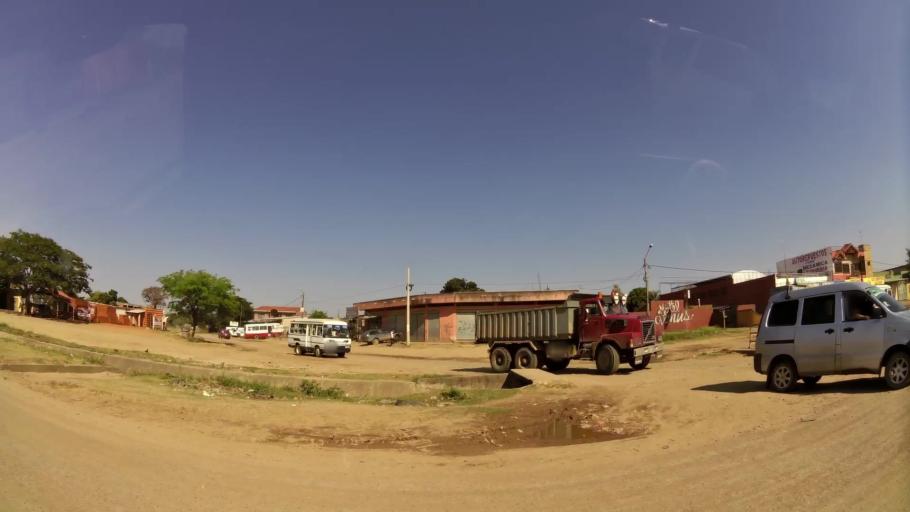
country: BO
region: Santa Cruz
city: Cotoca
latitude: -17.8162
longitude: -63.1146
